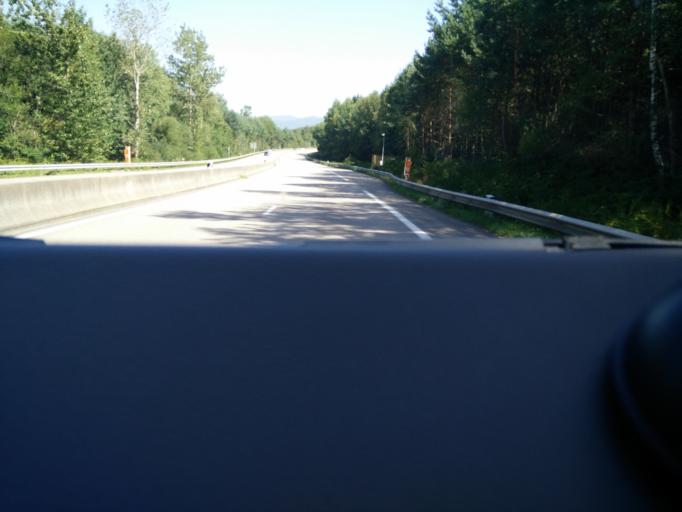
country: FR
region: Lorraine
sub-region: Departement des Vosges
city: Saint-Die-des-Vosges
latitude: 48.2629
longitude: 6.9518
